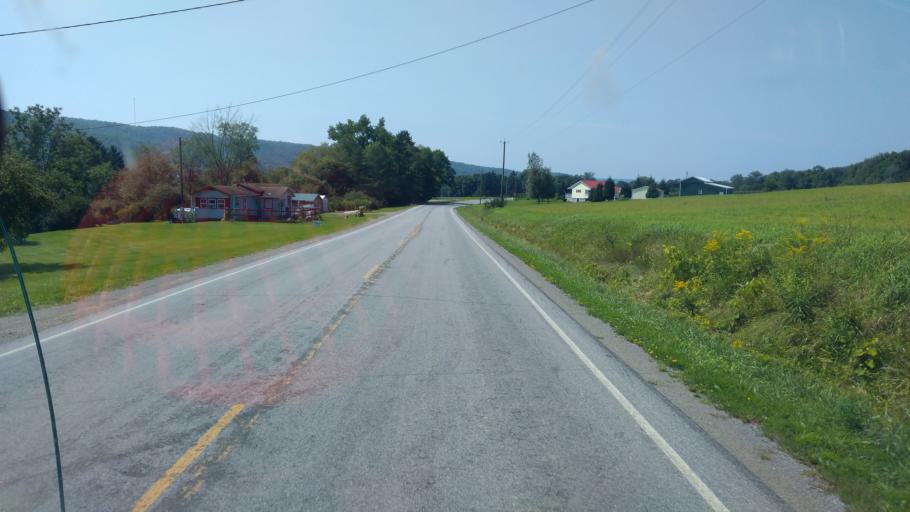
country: US
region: New York
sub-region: Allegany County
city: Belmont
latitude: 42.3036
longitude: -77.9694
